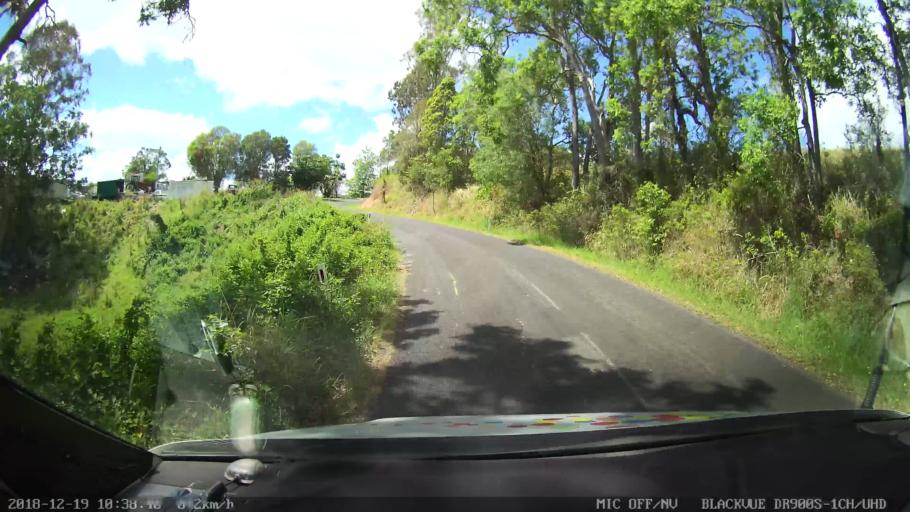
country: AU
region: New South Wales
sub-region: Lismore Municipality
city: Nimbin
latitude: -28.5762
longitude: 153.1550
